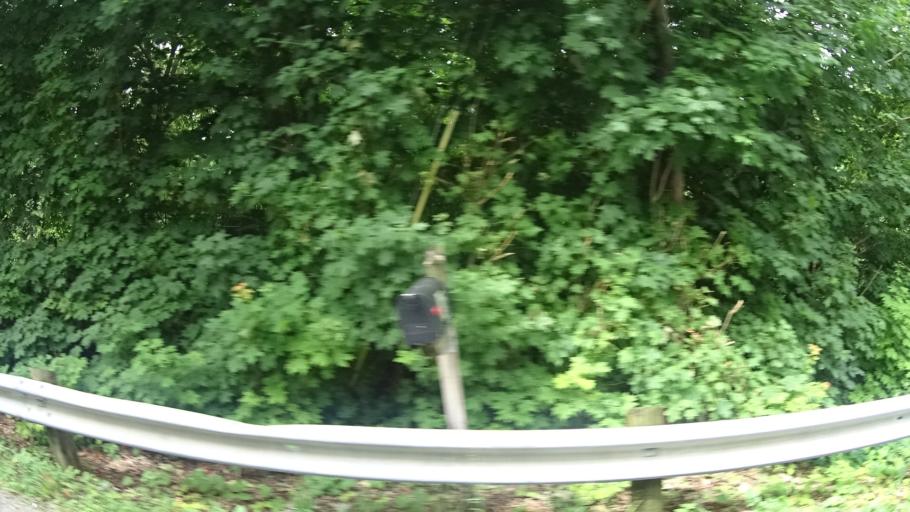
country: US
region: Ohio
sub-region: Erie County
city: Huron
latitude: 41.3261
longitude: -82.5020
